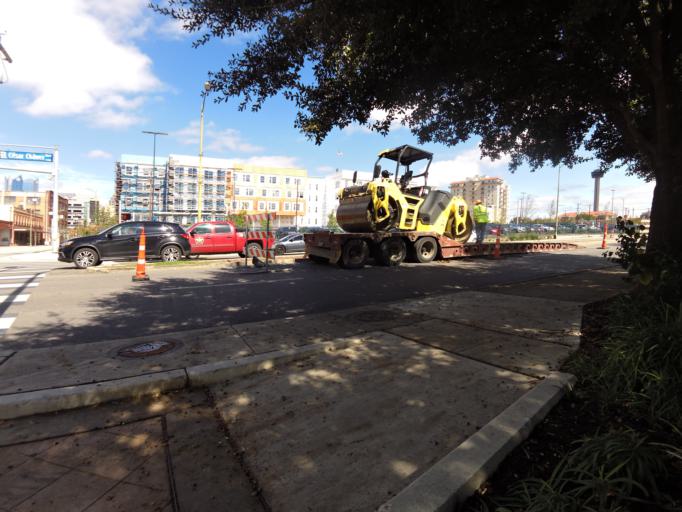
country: US
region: Texas
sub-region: Bexar County
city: San Antonio
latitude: 29.4198
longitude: -98.4964
